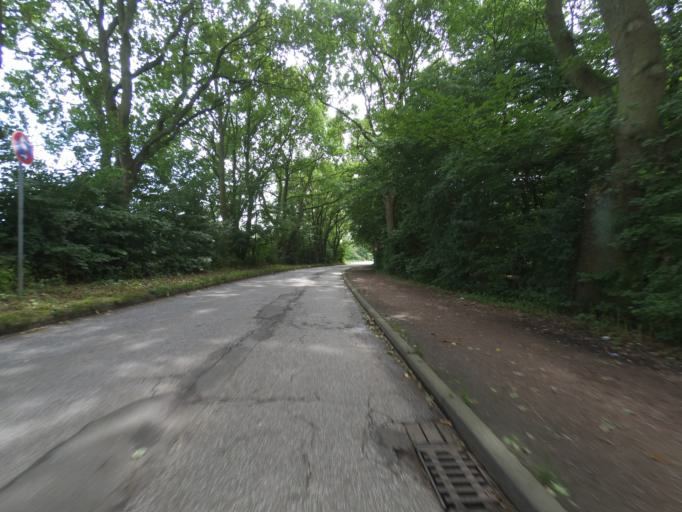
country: DE
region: Schleswig-Holstein
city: Oststeinbek
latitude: 53.5483
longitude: 10.1337
